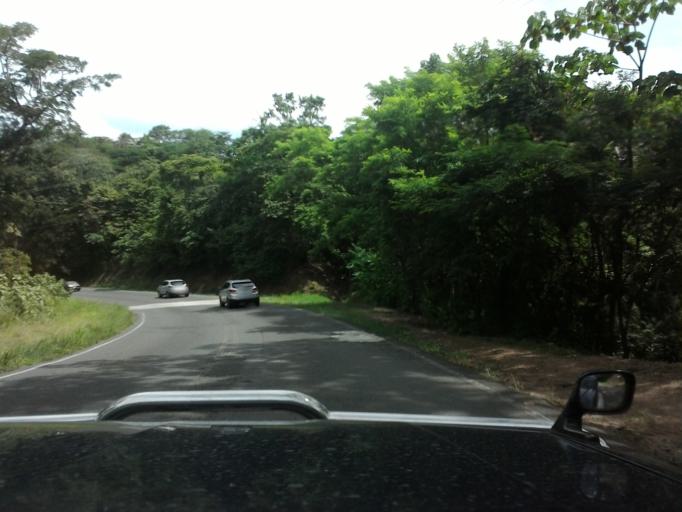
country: CR
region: Puntarenas
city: Esparza
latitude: 10.0187
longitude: -84.5987
